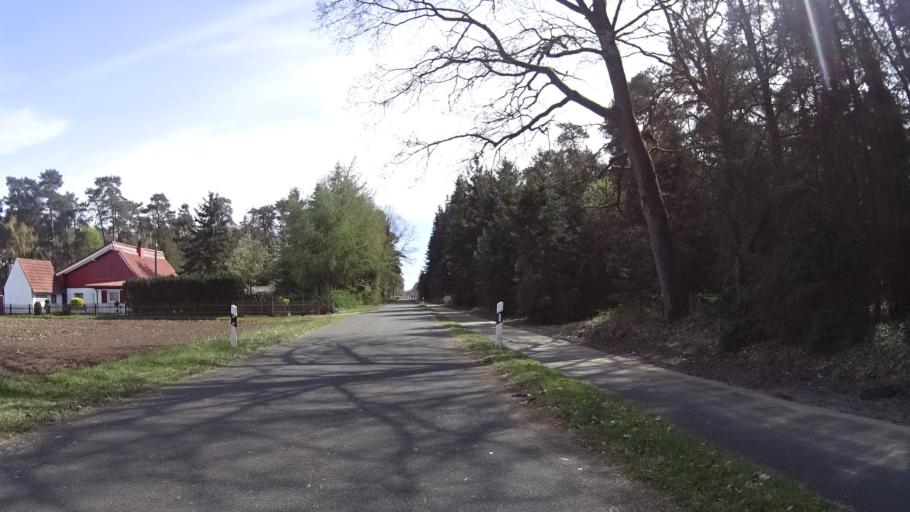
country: DE
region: Lower Saxony
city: Spelle
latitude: 52.3448
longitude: 7.4463
